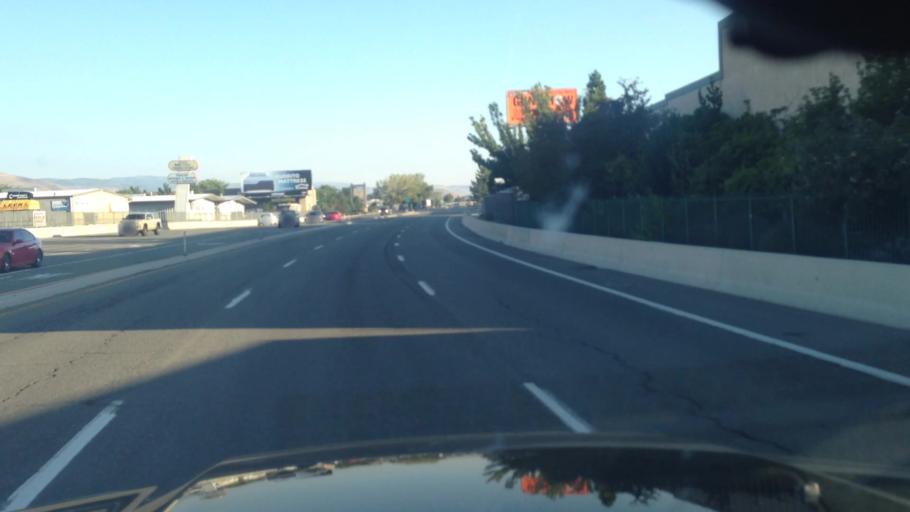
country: US
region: Nevada
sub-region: Washoe County
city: Sparks
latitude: 39.5268
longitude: -119.7398
